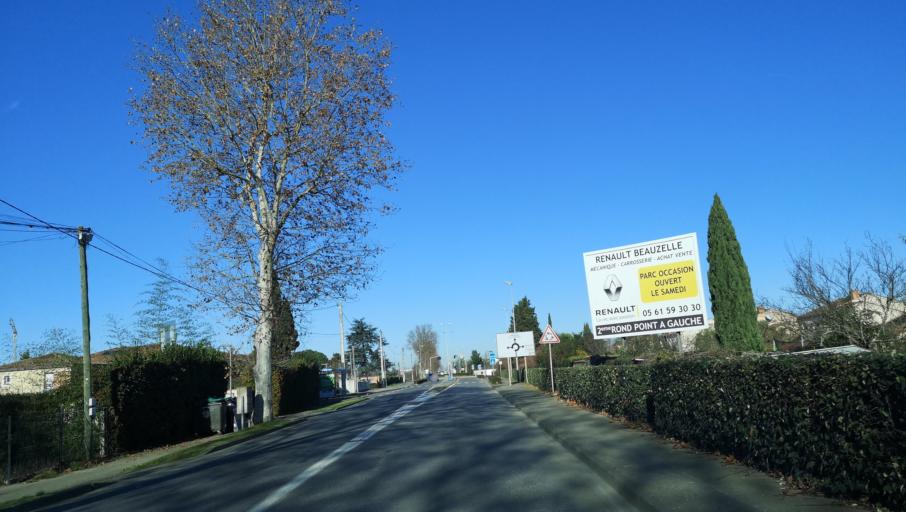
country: FR
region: Midi-Pyrenees
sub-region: Departement de la Haute-Garonne
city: Beauzelle
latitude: 43.6622
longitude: 1.3733
